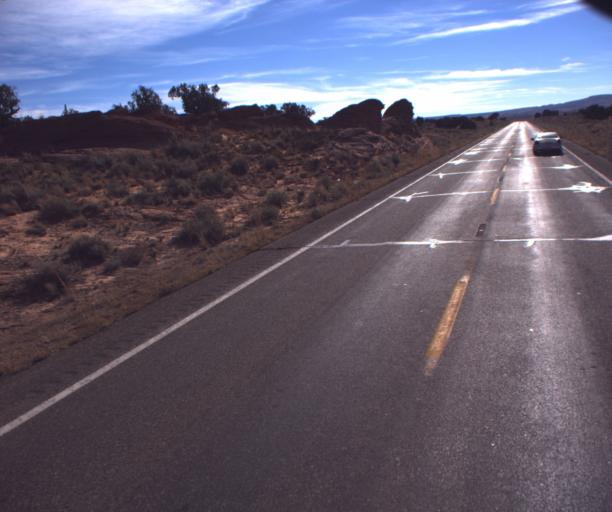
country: US
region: Arizona
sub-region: Coconino County
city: Kaibito
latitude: 36.6335
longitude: -111.2103
